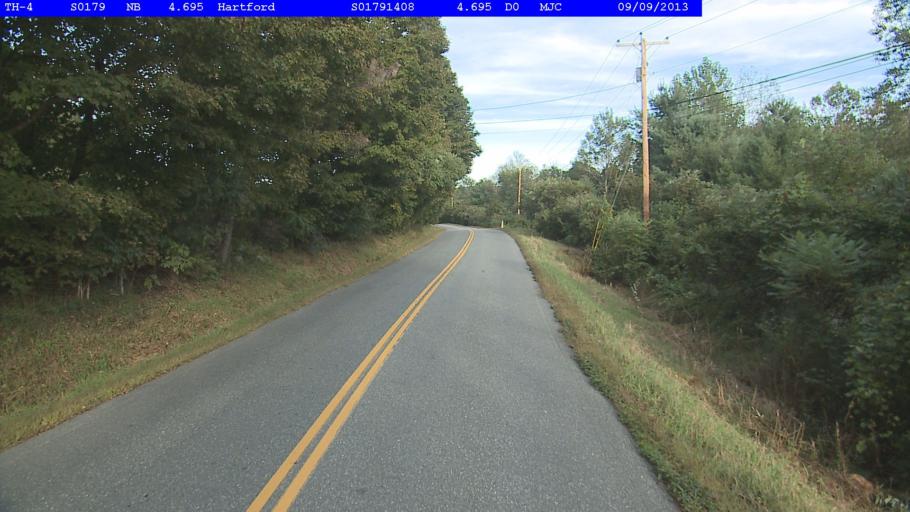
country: US
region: Vermont
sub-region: Windsor County
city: White River Junction
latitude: 43.7007
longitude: -72.4249
